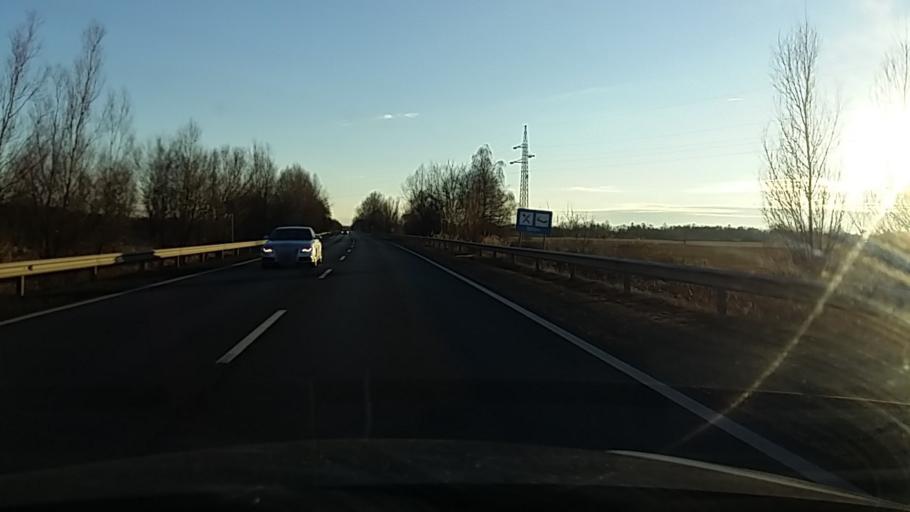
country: HU
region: Szabolcs-Szatmar-Bereg
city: Ujfeherto
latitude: 47.8748
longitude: 21.7057
